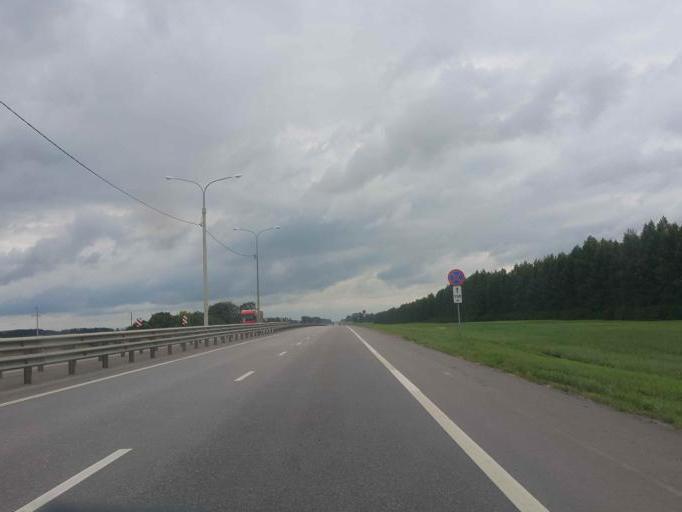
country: RU
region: Tambov
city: Zavoronezhskoye
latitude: 52.8445
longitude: 40.8265
